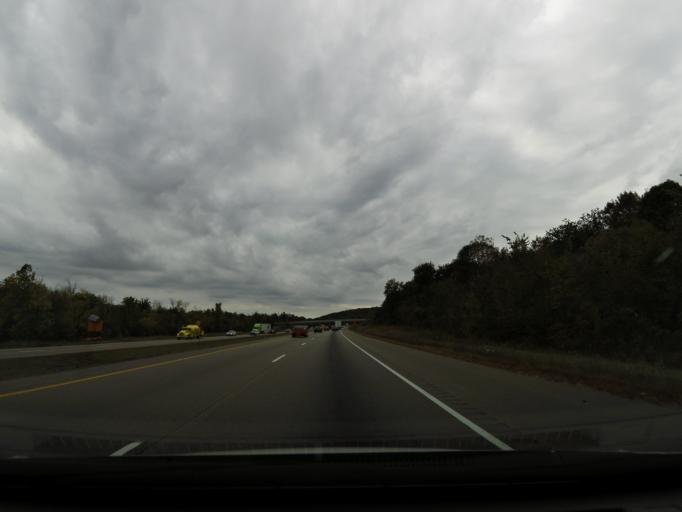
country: CA
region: Ontario
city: Quinte West
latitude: 44.1036
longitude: -77.6802
